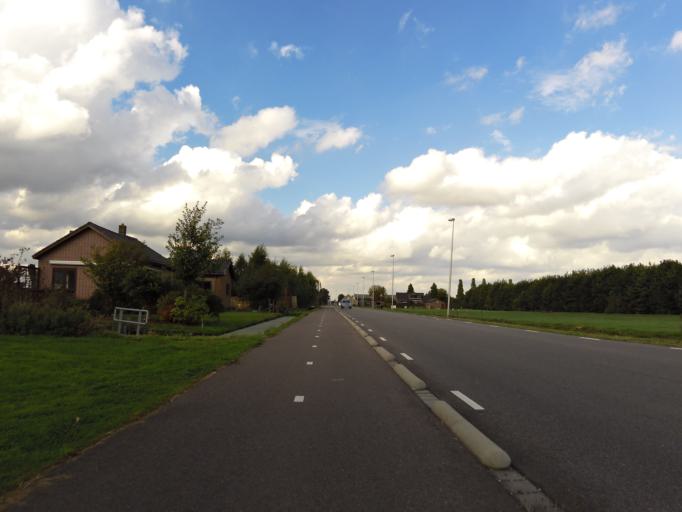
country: NL
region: South Holland
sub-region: Gemeente Boskoop
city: Boskoop
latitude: 52.0804
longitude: 4.6331
